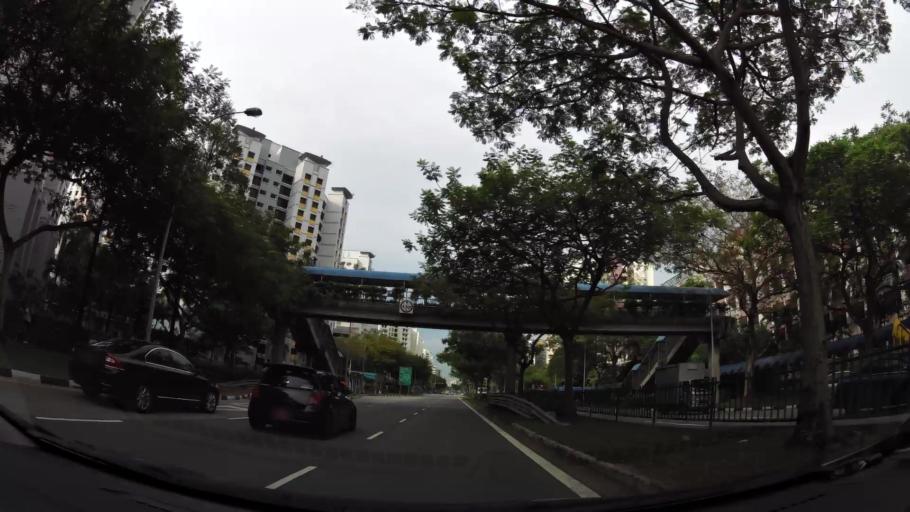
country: MY
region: Johor
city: Kampung Pasir Gudang Baru
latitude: 1.3875
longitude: 103.8917
